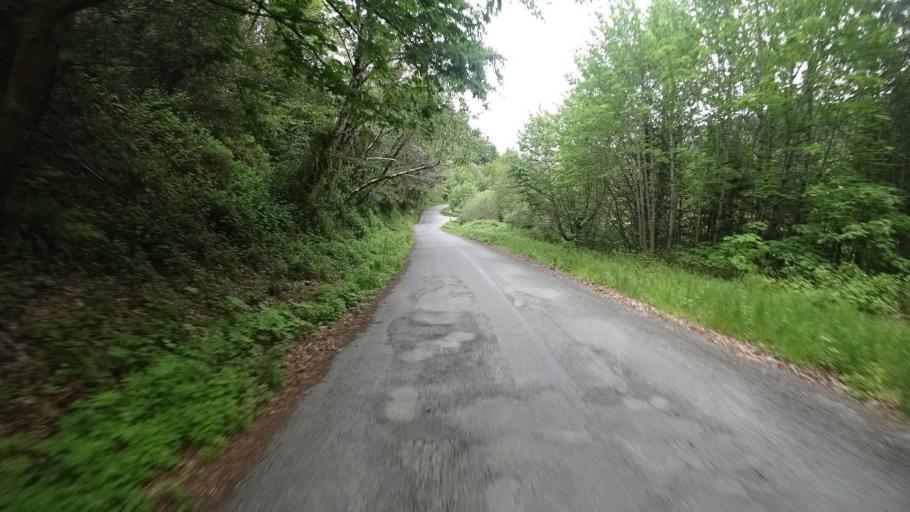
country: US
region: California
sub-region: Humboldt County
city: Willow Creek
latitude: 41.2064
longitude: -123.7576
